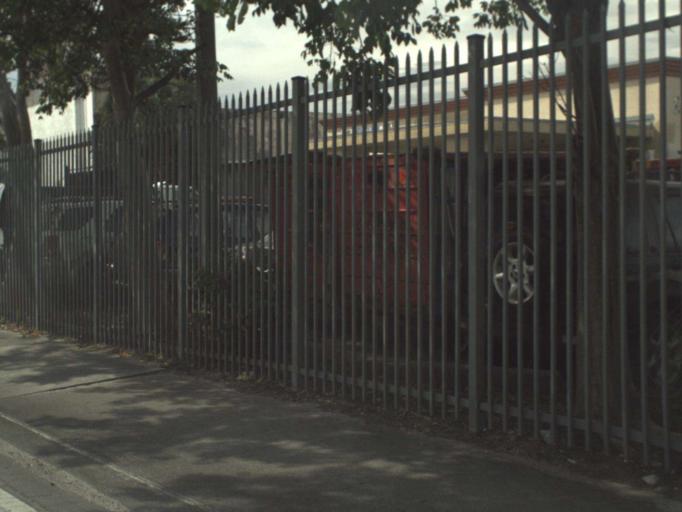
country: US
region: Florida
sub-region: Miami-Dade County
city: Westview
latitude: 25.8830
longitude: -80.2329
